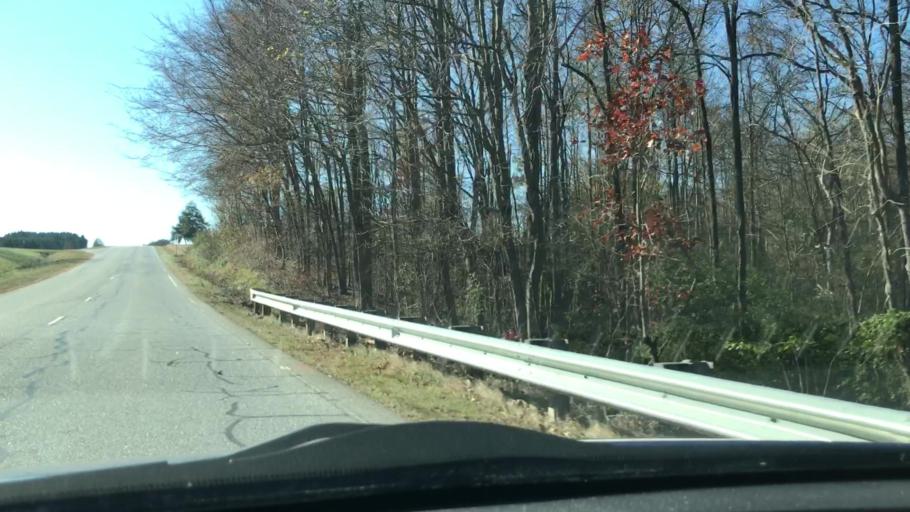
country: US
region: North Carolina
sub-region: Davidson County
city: Denton
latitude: 35.5905
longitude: -80.0479
